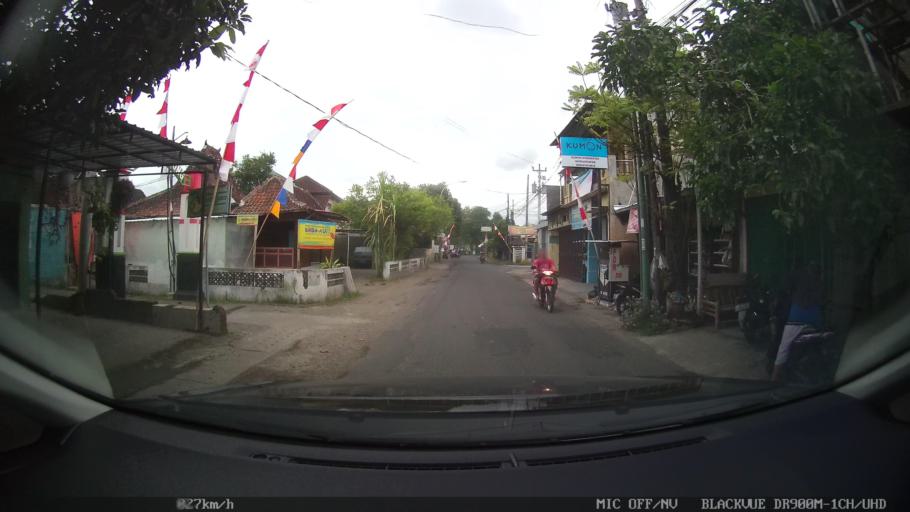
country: ID
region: Daerah Istimewa Yogyakarta
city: Sewon
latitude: -7.8451
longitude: 110.4020
